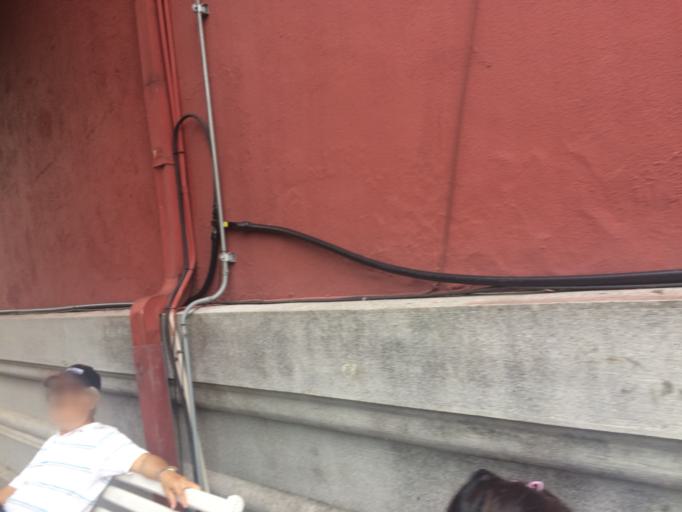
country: TW
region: Taipei
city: Taipei
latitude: 25.0316
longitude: 121.5110
